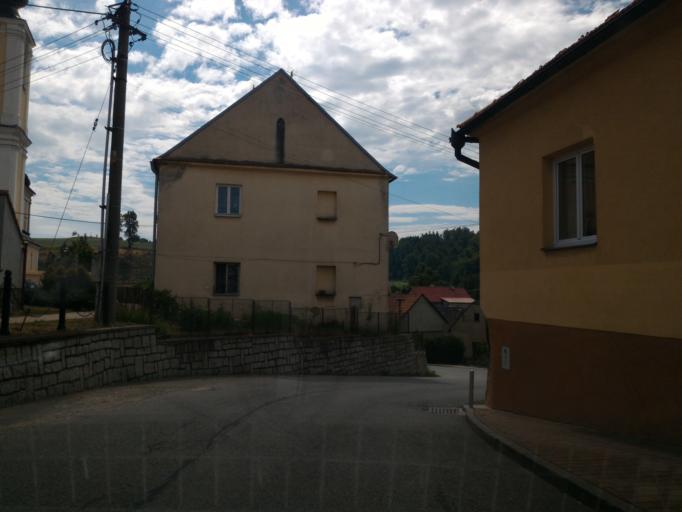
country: CZ
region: Vysocina
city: Zeletava
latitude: 49.1390
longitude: 15.5637
